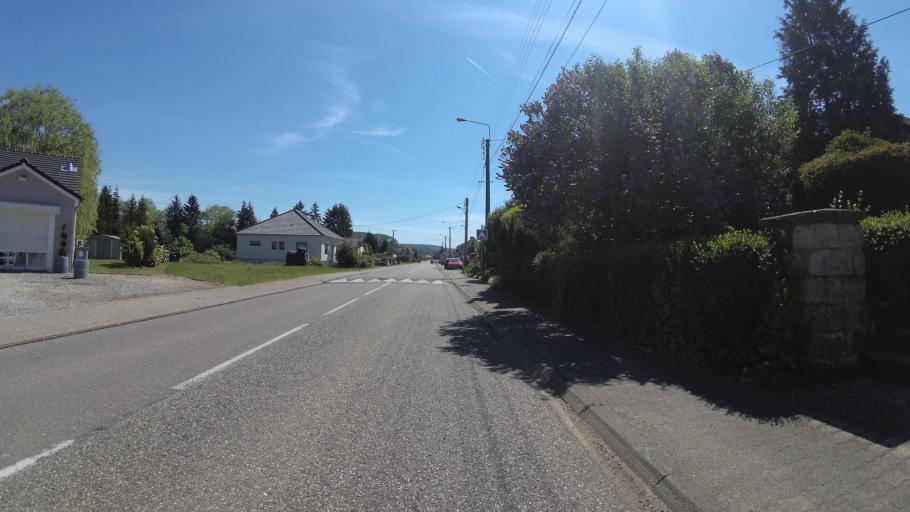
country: FR
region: Lorraine
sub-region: Departement de la Moselle
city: Sarreinsming
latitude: 49.1265
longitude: 7.1329
